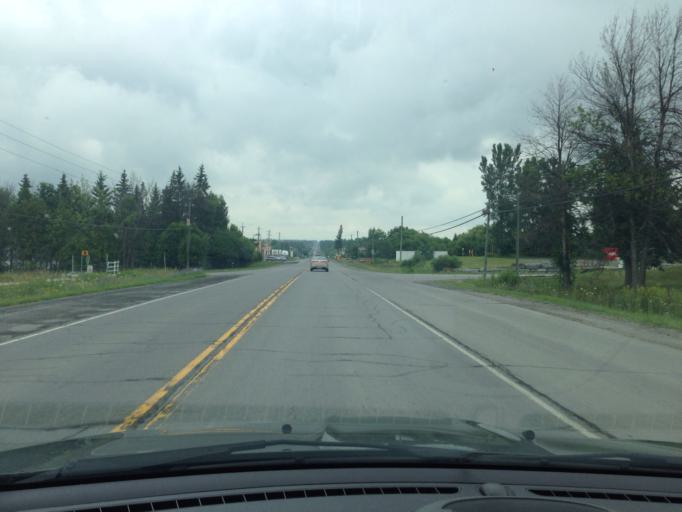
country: CA
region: Ontario
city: Ottawa
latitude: 45.3013
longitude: -75.5826
